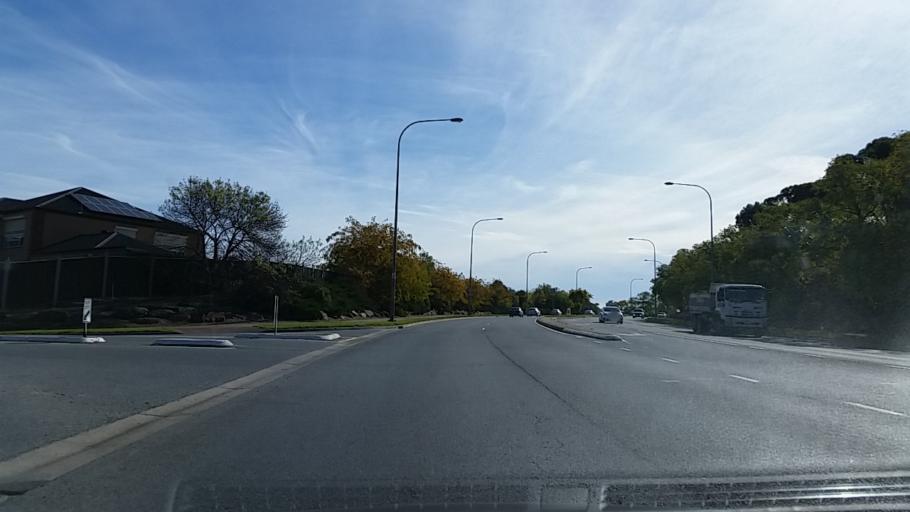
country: AU
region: South Australia
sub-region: Tea Tree Gully
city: Golden Grove
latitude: -34.7954
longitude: 138.7006
